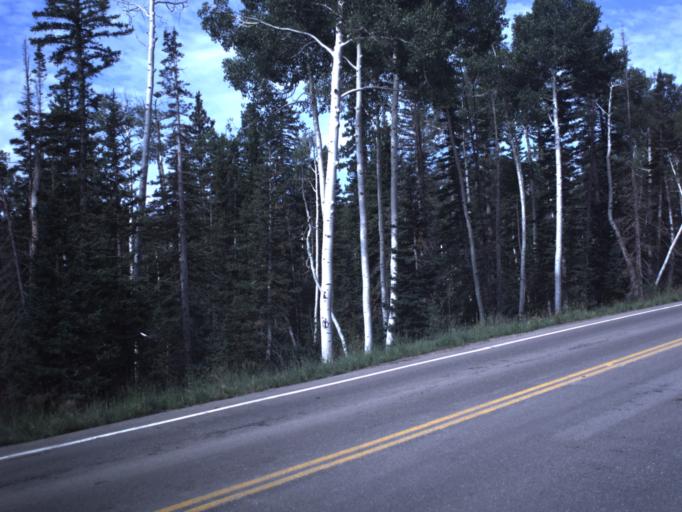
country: US
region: Utah
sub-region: Iron County
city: Parowan
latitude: 37.5228
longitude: -112.7380
